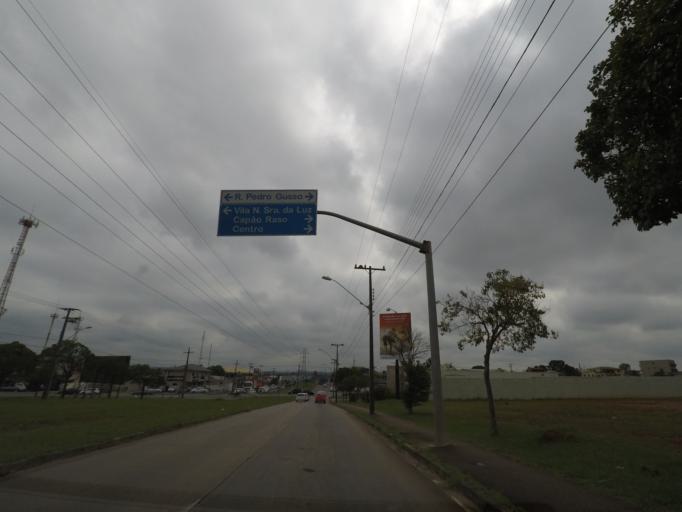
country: BR
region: Parana
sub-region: Curitiba
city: Curitiba
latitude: -25.5044
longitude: -49.3142
